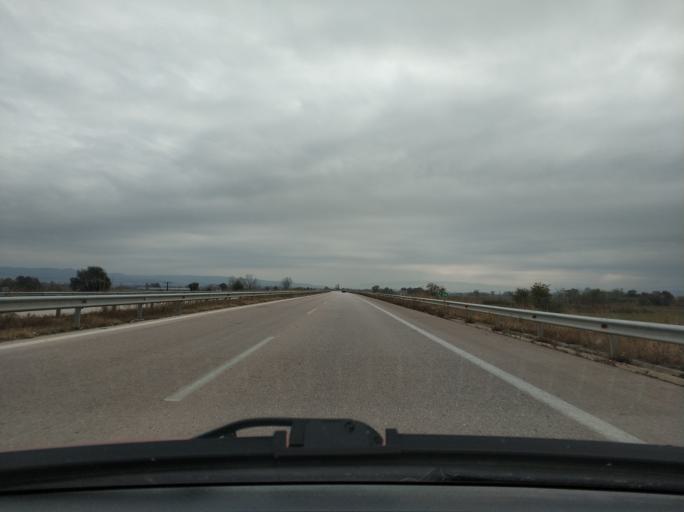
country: GR
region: Central Macedonia
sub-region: Nomos Thessalonikis
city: Lagkadas
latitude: 40.7280
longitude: 23.0677
